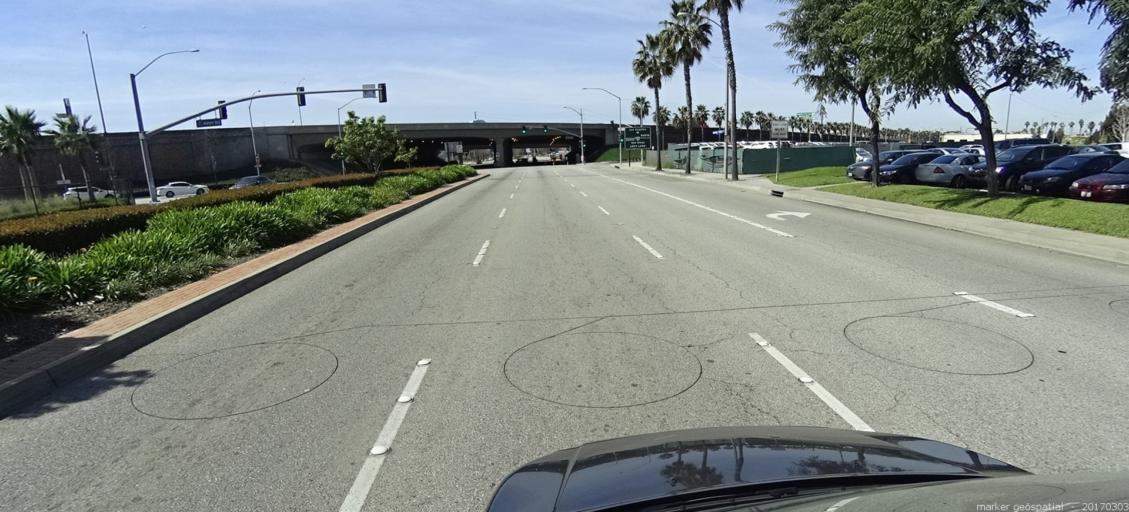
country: US
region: California
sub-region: Orange County
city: Orange
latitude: 33.7962
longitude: -117.8930
